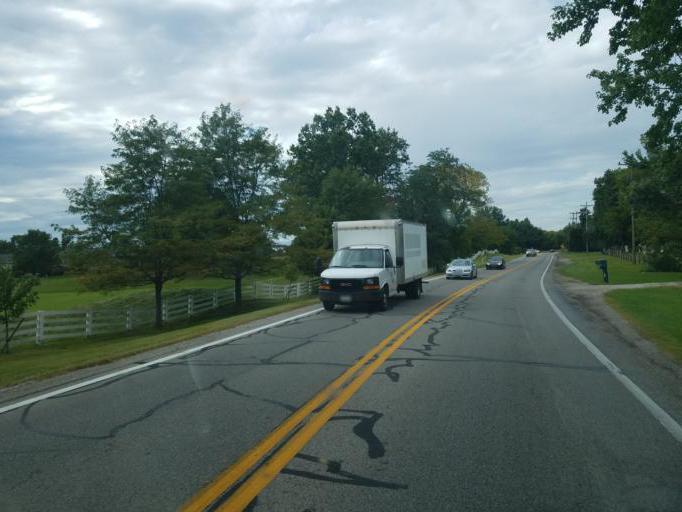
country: US
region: Ohio
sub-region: Franklin County
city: Reynoldsburg
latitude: 40.0152
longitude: -82.8130
